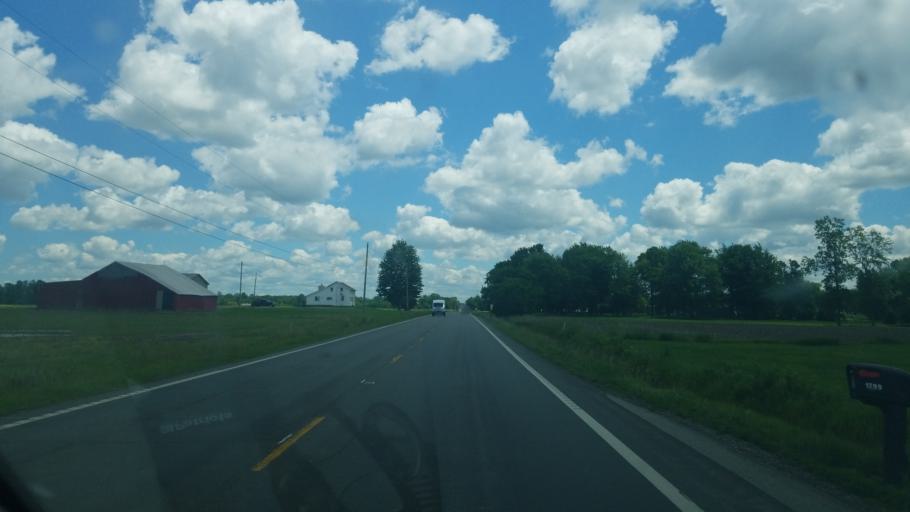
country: US
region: Ohio
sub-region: Huron County
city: New London
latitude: 41.0296
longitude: -82.3785
